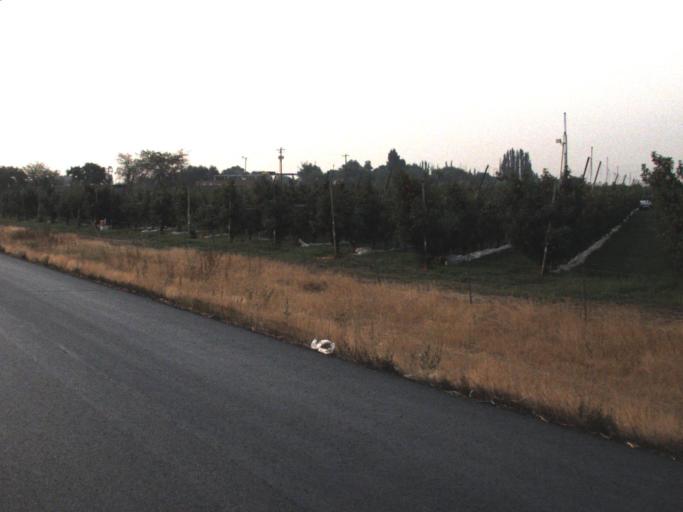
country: US
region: Washington
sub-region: Yakima County
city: Wapato
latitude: 46.4373
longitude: -120.4240
